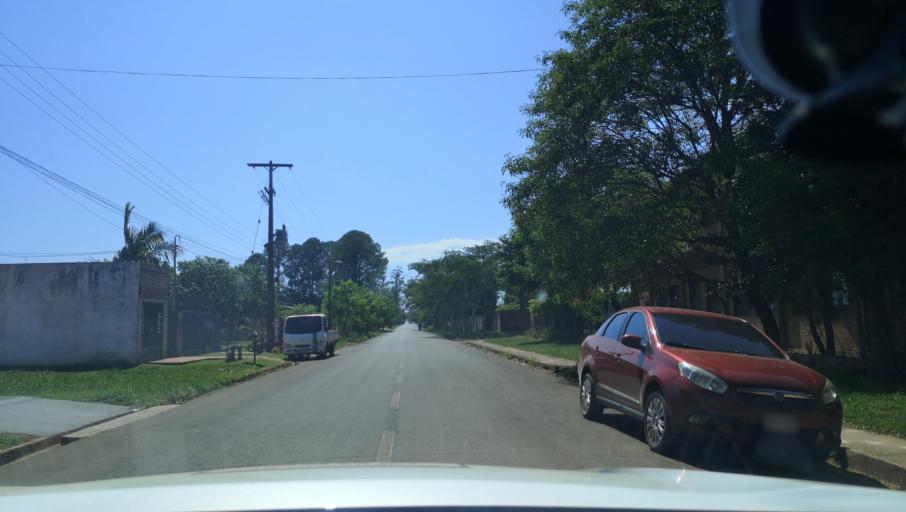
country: PY
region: Itapua
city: Carmen del Parana
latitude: -27.1595
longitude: -56.2443
